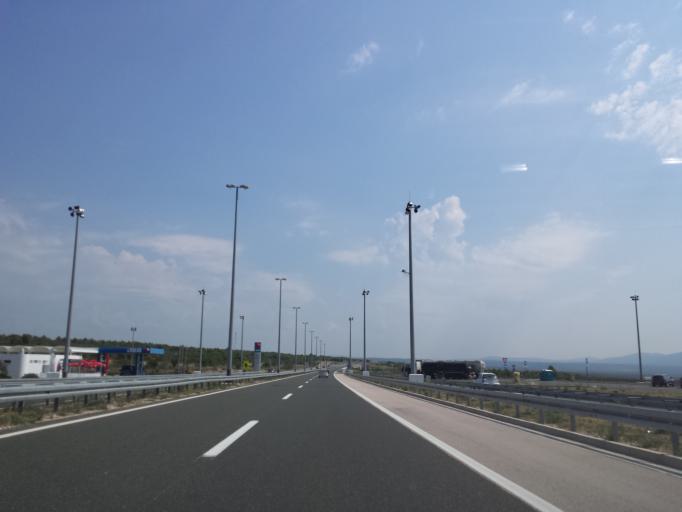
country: HR
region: Sibensko-Kniniska
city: Zaton
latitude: 43.8563
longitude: 15.8452
